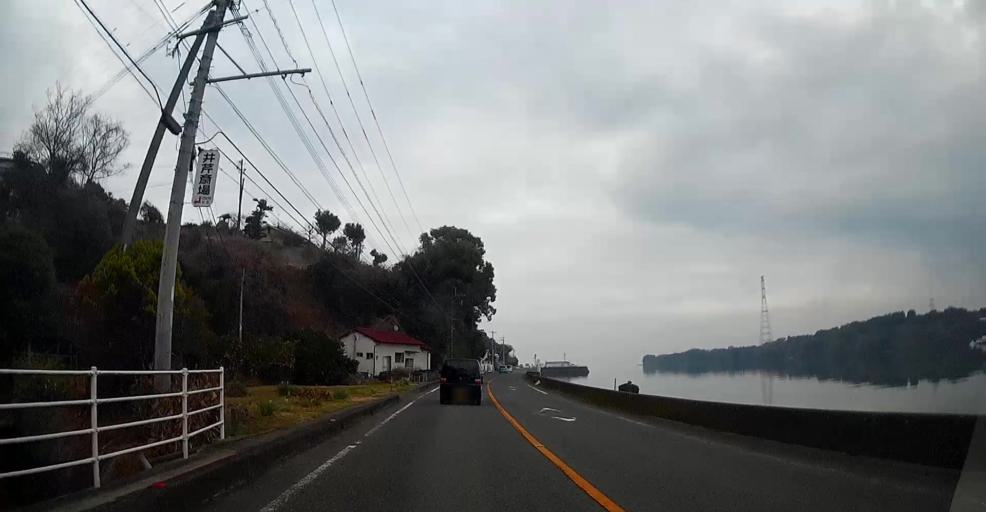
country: JP
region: Kumamoto
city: Yatsushiro
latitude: 32.6124
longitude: 130.4955
